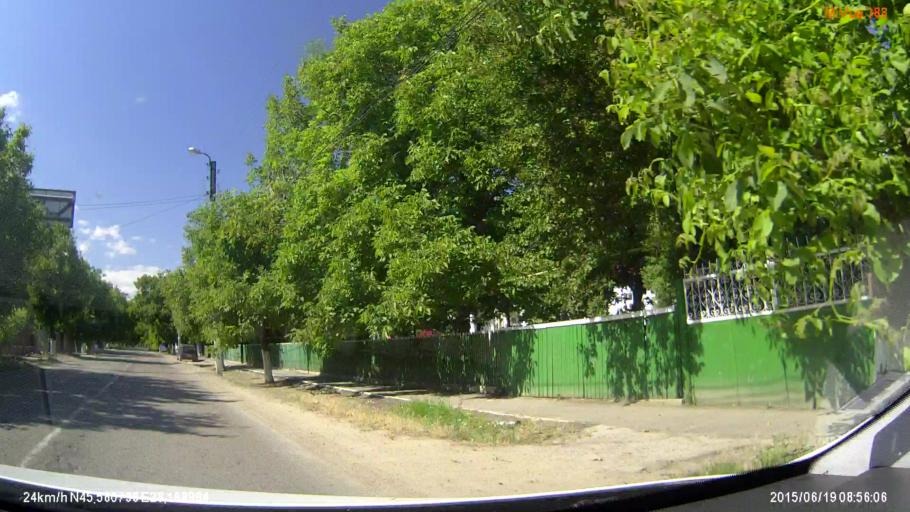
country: MD
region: Cahul
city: Giurgiulesti
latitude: 45.5807
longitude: 28.1690
